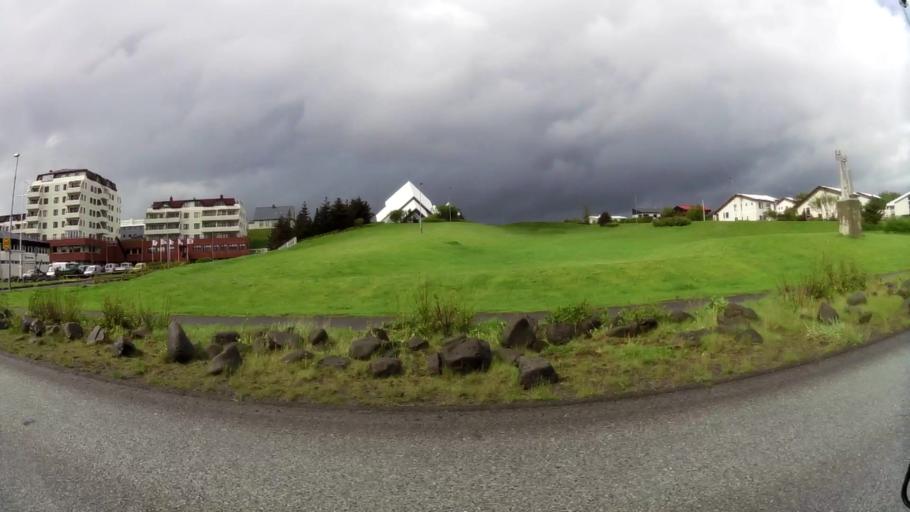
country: IS
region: Capital Region
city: Seltjarnarnes
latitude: 64.1535
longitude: -21.9864
